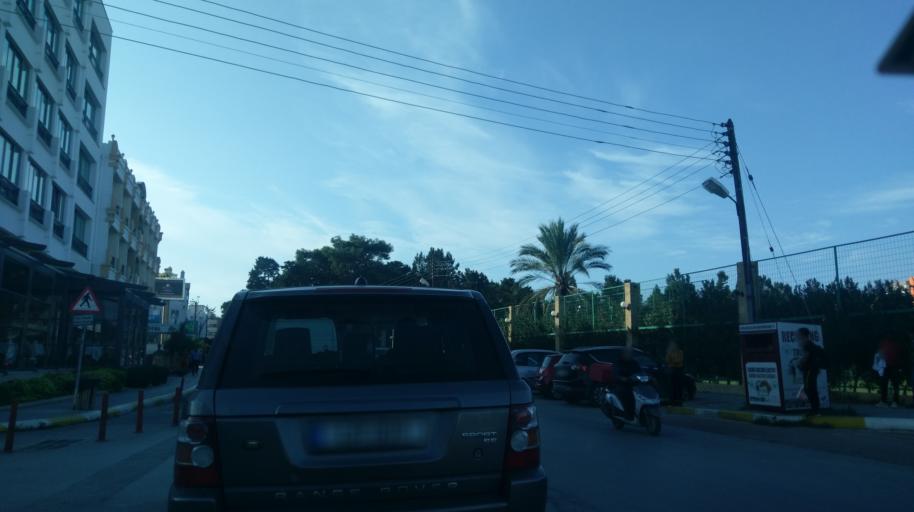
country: CY
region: Keryneia
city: Kyrenia
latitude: 35.3342
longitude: 33.3302
